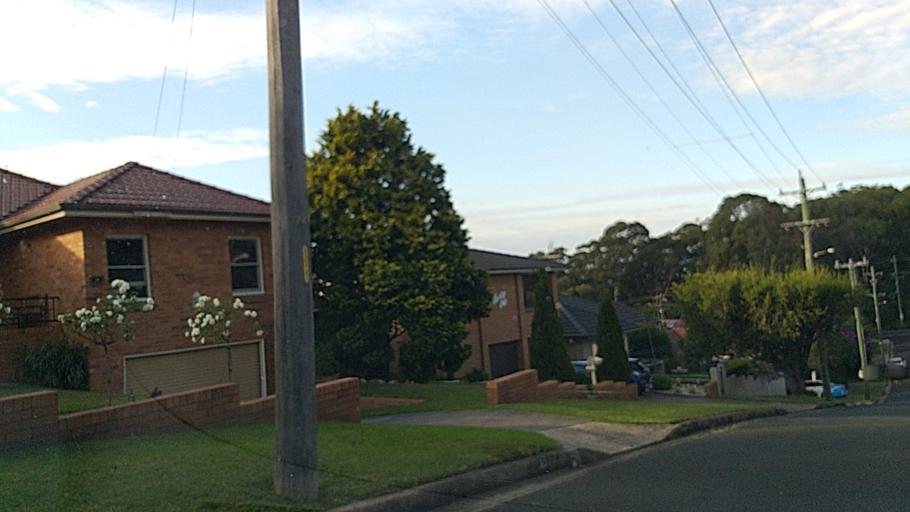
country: AU
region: New South Wales
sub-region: Wollongong
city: Mount Ousley
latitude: -34.4005
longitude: 150.8839
